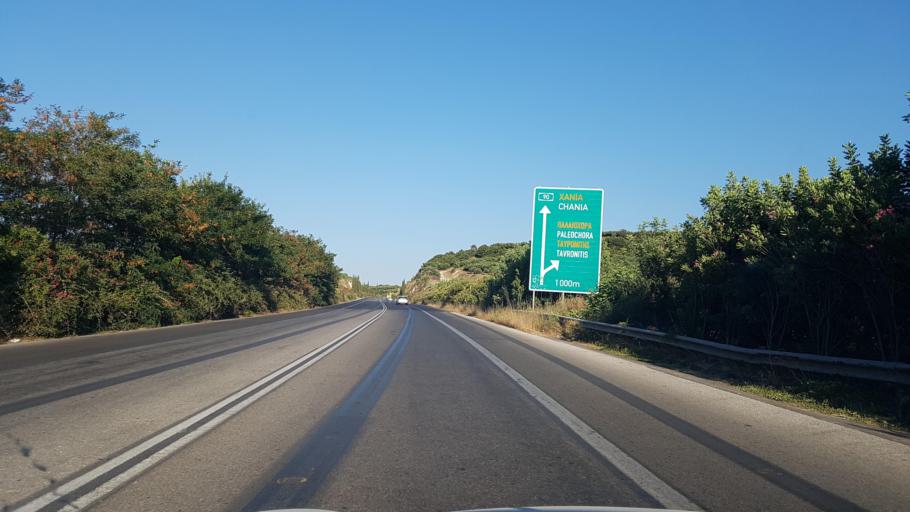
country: GR
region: Crete
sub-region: Nomos Chanias
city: Kolympari
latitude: 35.5243
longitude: 23.8055
